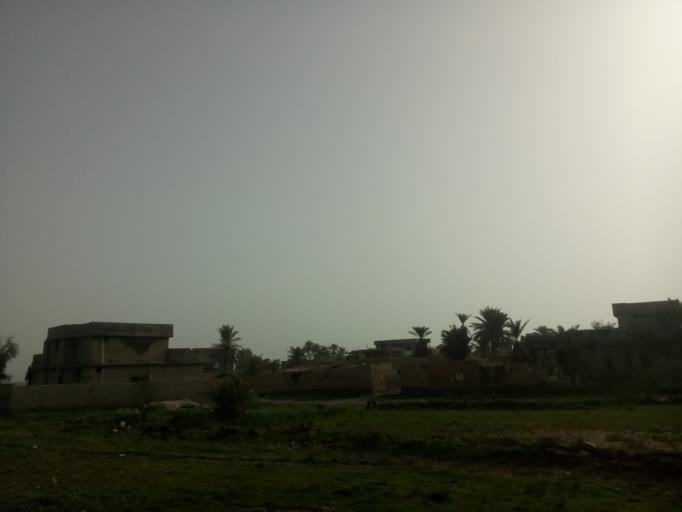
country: IQ
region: Salah ad Din Governorate
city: Tozkhurmato
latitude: 34.7809
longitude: 44.5767
